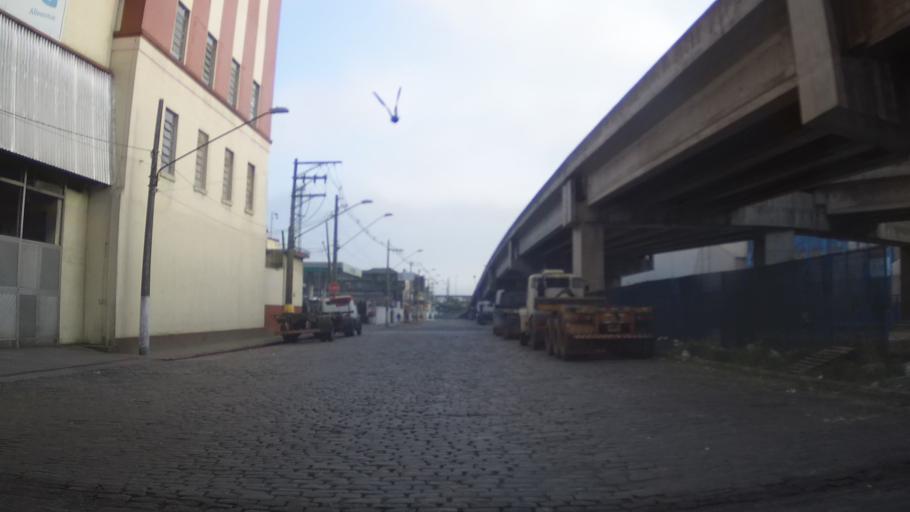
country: BR
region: Sao Paulo
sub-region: Santos
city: Santos
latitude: -23.9379
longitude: -46.3159
